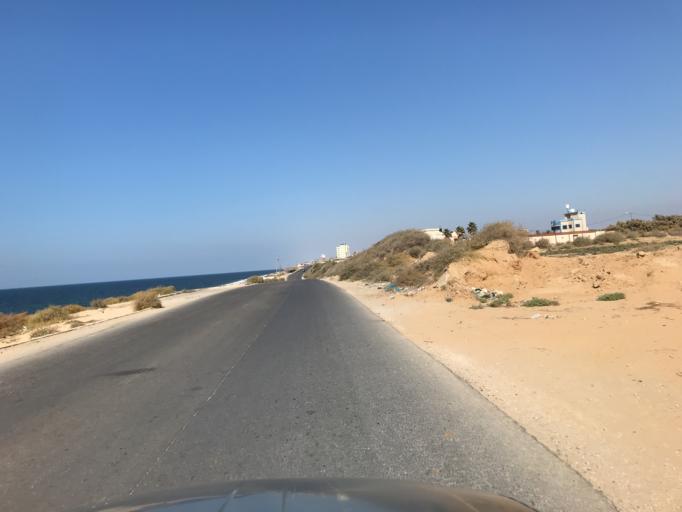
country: PS
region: Gaza Strip
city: Dayr al Balah
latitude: 31.4413
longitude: 34.3543
